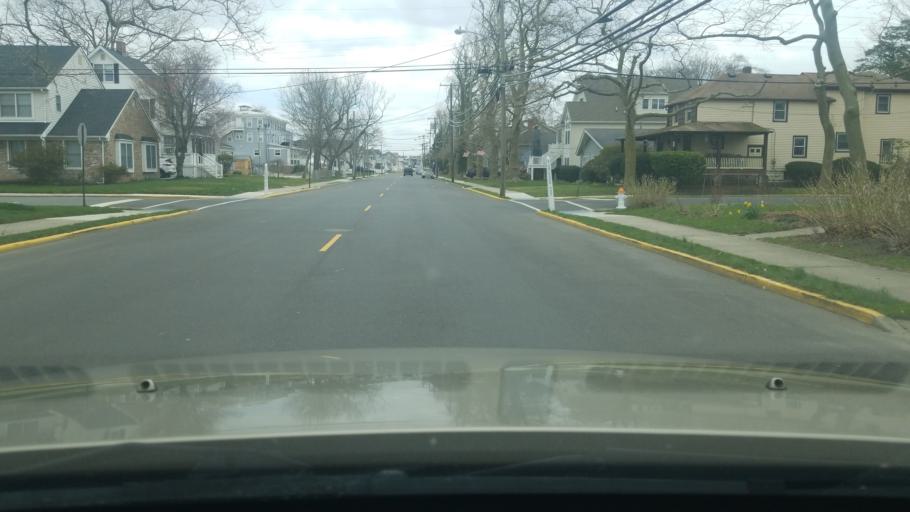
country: US
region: New Jersey
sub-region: Monmouth County
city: Manasquan
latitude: 40.1174
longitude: -74.0416
